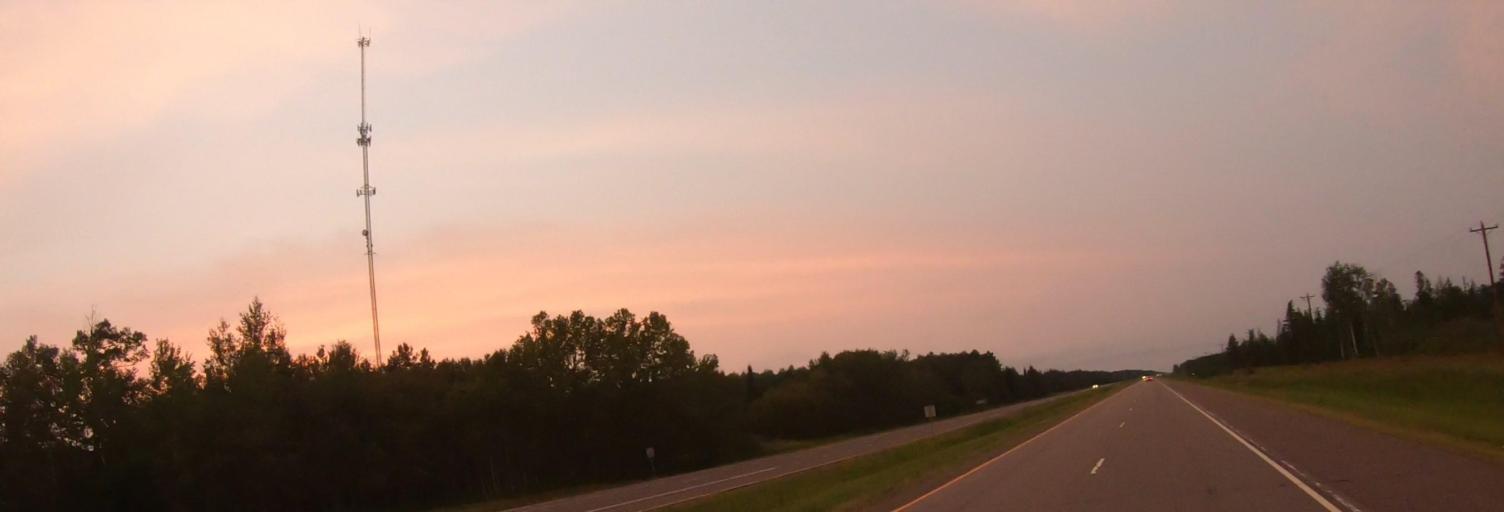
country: US
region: Minnesota
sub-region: Carlton County
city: Cloquet
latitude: 47.0690
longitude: -92.4713
